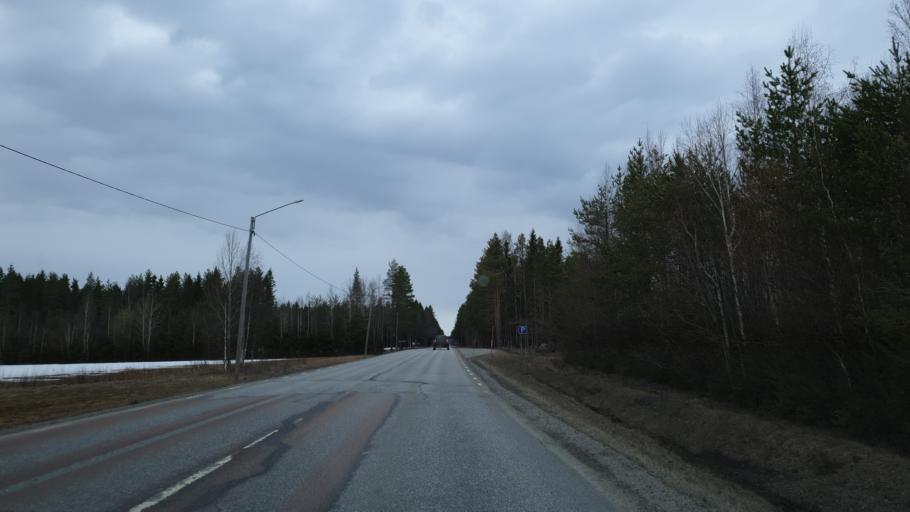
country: SE
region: Vaesterbotten
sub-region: Skelleftea Kommun
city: Viken
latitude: 64.6507
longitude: 20.9557
